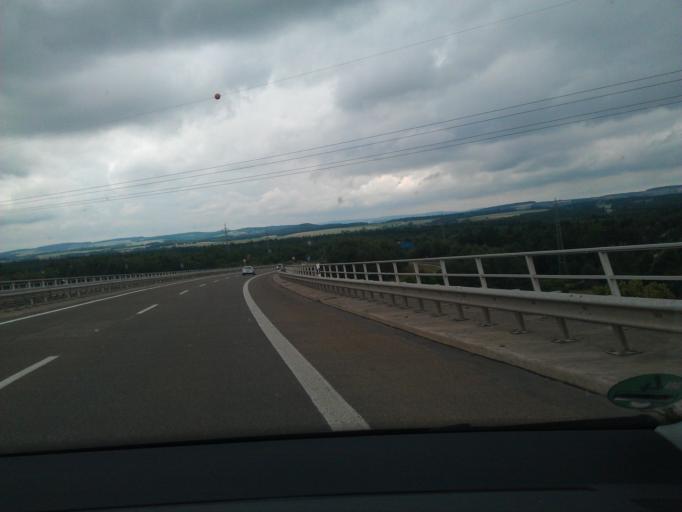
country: DE
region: Rheinland-Pfalz
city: Landstuhl
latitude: 49.4098
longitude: 7.5371
